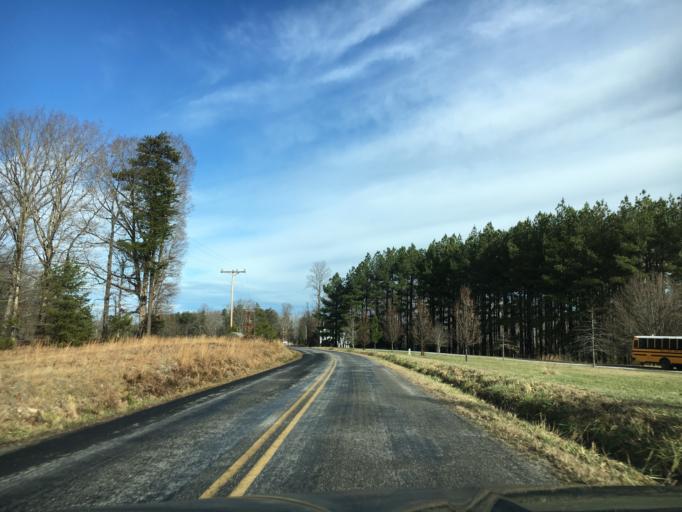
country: US
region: Virginia
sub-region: Nottoway County
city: Crewe
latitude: 37.3042
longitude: -78.1955
